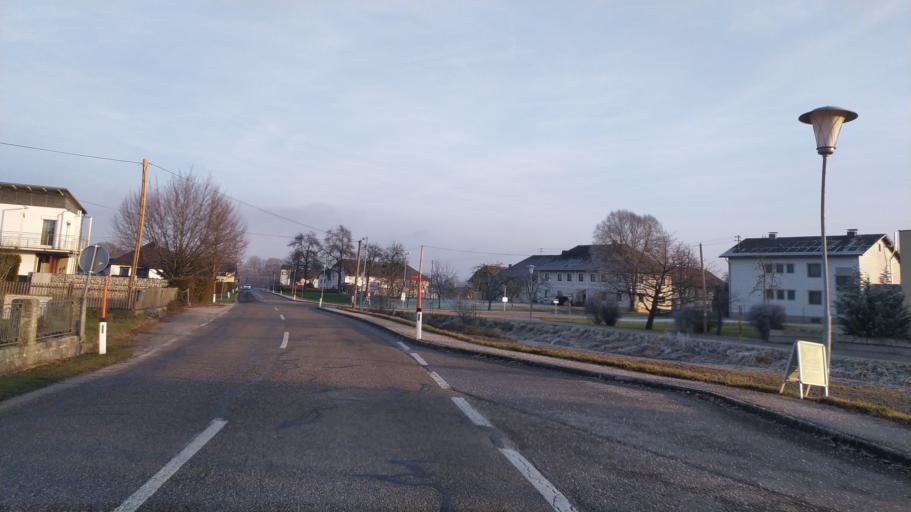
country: AT
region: Upper Austria
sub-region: Politischer Bezirk Urfahr-Umgebung
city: Goldworth
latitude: 48.3313
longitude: 14.0984
